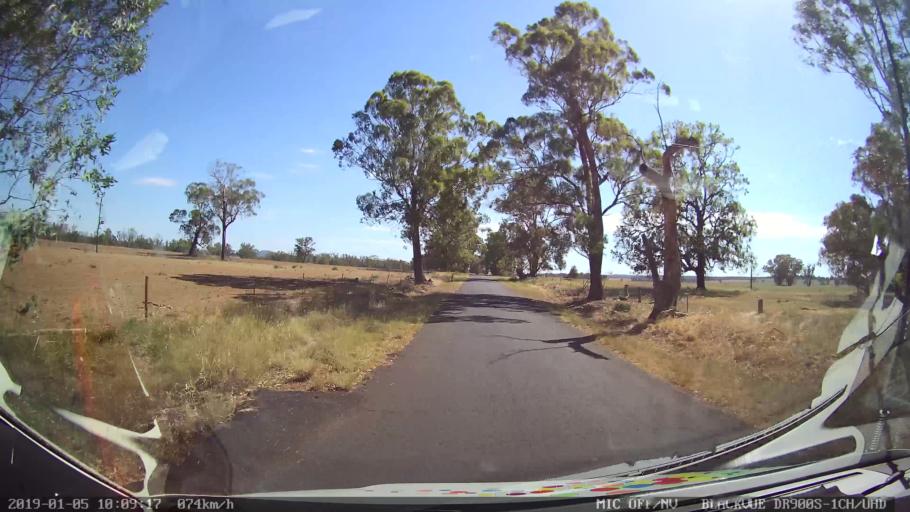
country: AU
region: New South Wales
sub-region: Gilgandra
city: Gilgandra
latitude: -31.6327
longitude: 148.8856
